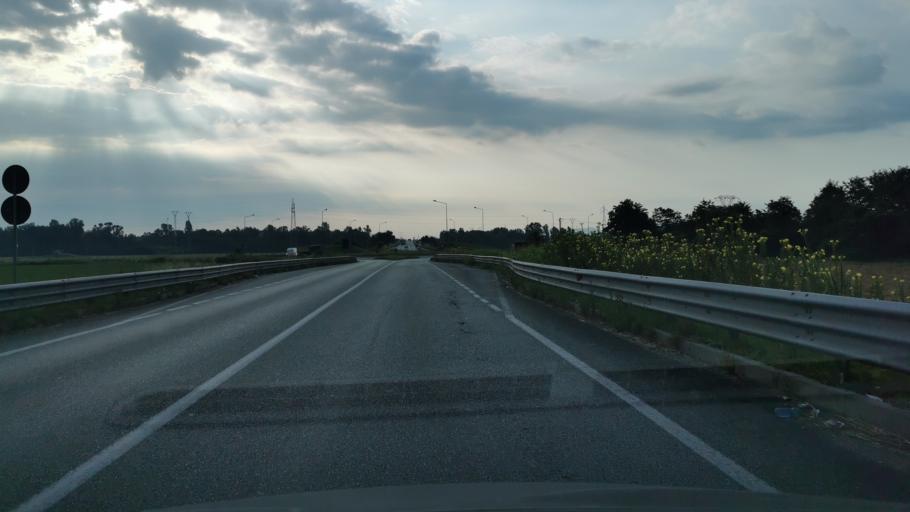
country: IT
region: Piedmont
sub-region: Provincia di Torino
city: Borgaro Torinese
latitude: 45.1504
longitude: 7.6318
